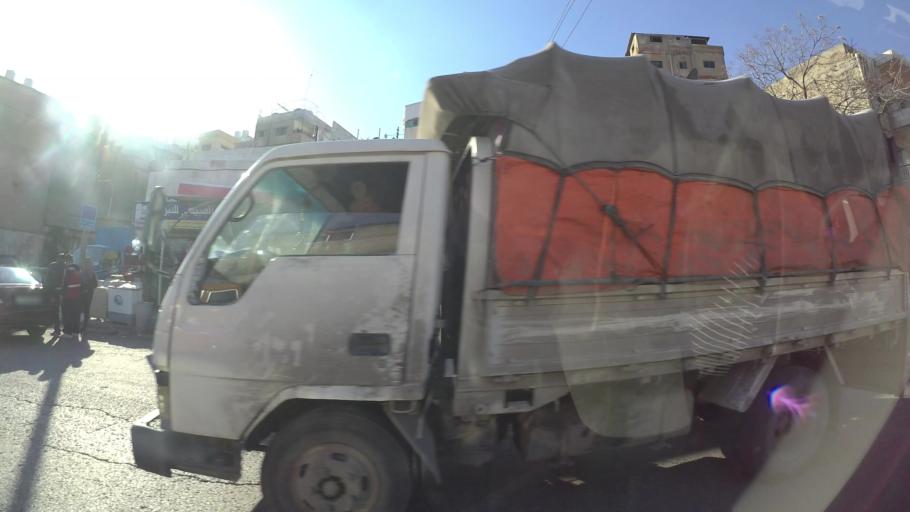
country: JO
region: Amman
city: Amman
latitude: 31.9671
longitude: 35.9605
